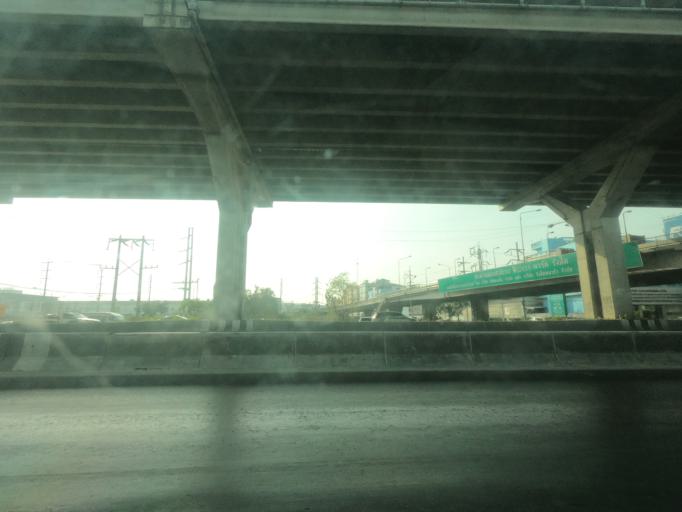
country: TH
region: Bangkok
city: Sai Mai
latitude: 13.9581
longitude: 100.6822
